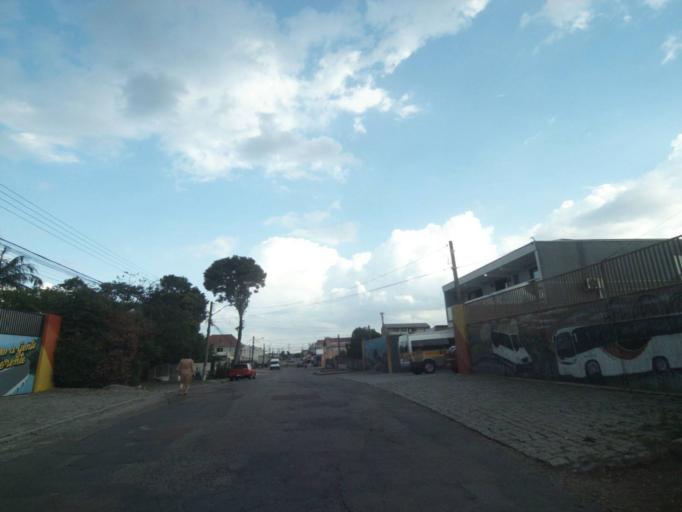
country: BR
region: Parana
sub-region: Sao Jose Dos Pinhais
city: Sao Jose dos Pinhais
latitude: -25.5348
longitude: -49.2760
